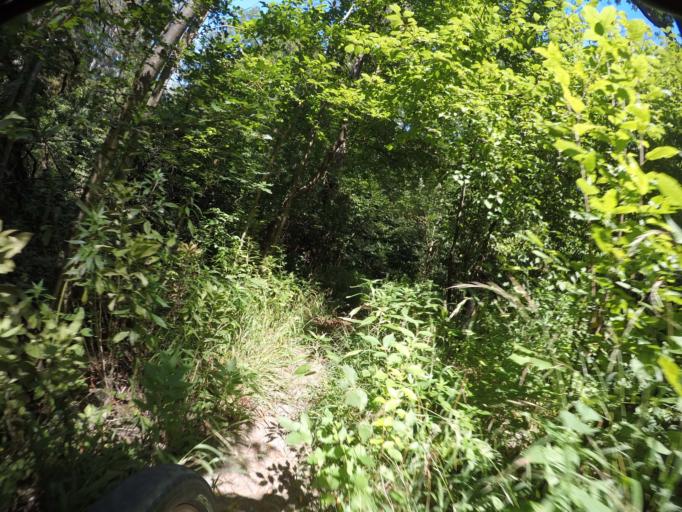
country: AT
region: Lower Austria
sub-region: Politischer Bezirk Ganserndorf
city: Gross-Enzersdorf
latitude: 48.1933
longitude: 16.4914
